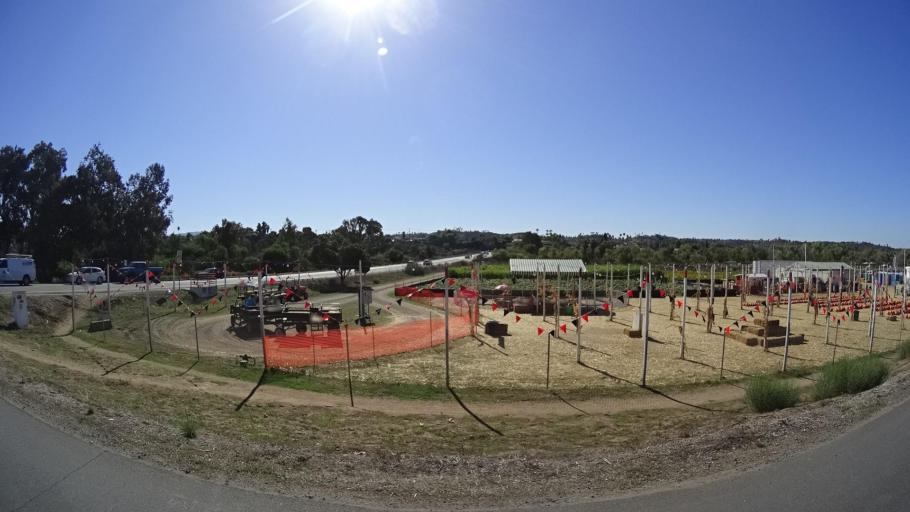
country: US
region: California
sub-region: San Diego County
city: Bonita
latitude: 32.6779
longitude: -117.0180
